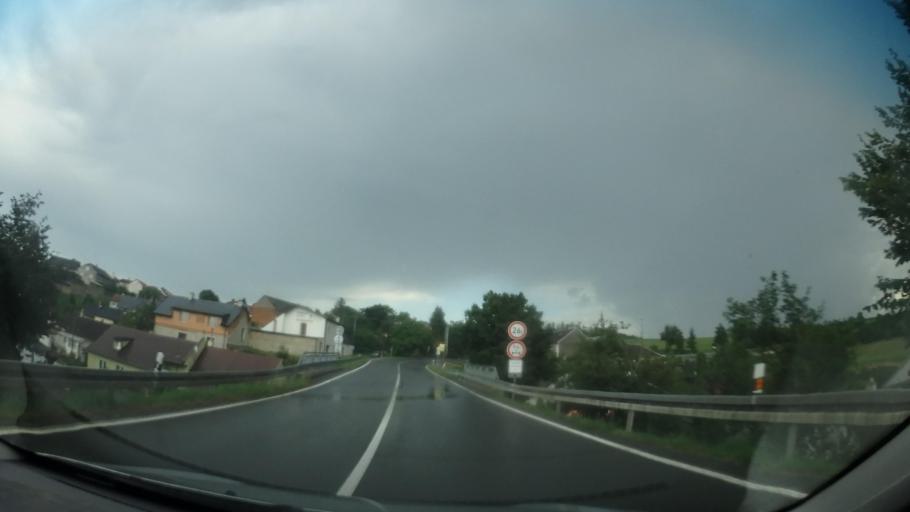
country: CZ
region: Olomoucky
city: Bila Lhota
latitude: 49.7111
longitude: 16.9828
